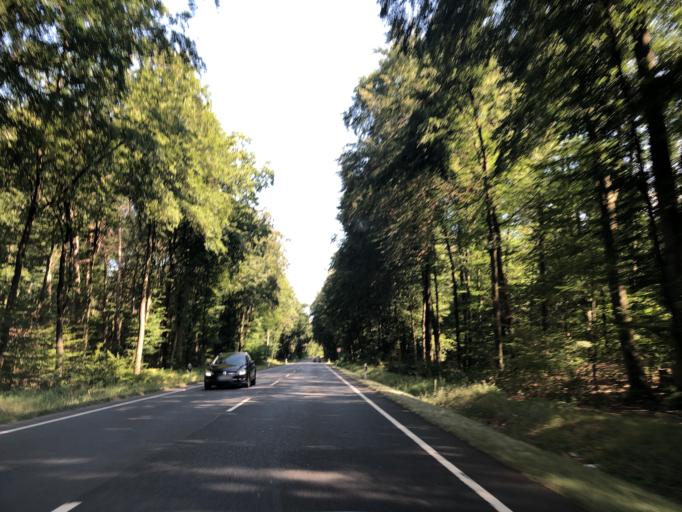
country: DE
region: Hesse
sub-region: Regierungsbezirk Darmstadt
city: Dietzenbach
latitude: 50.0437
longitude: 8.7596
